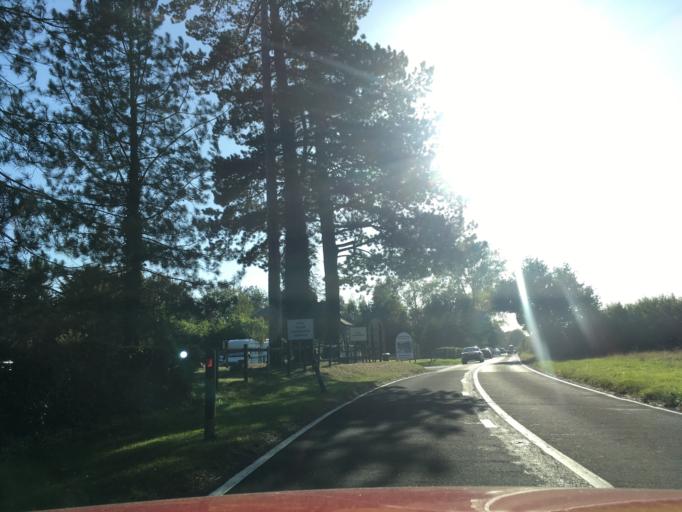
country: GB
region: England
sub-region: Hampshire
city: Swanmore
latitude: 50.9254
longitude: -1.1529
